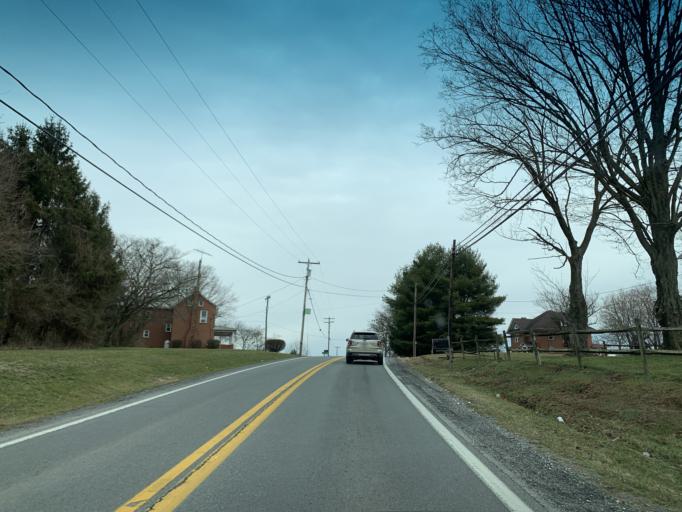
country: US
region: Maryland
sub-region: Washington County
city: Williamsport
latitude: 39.5953
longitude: -77.8453
